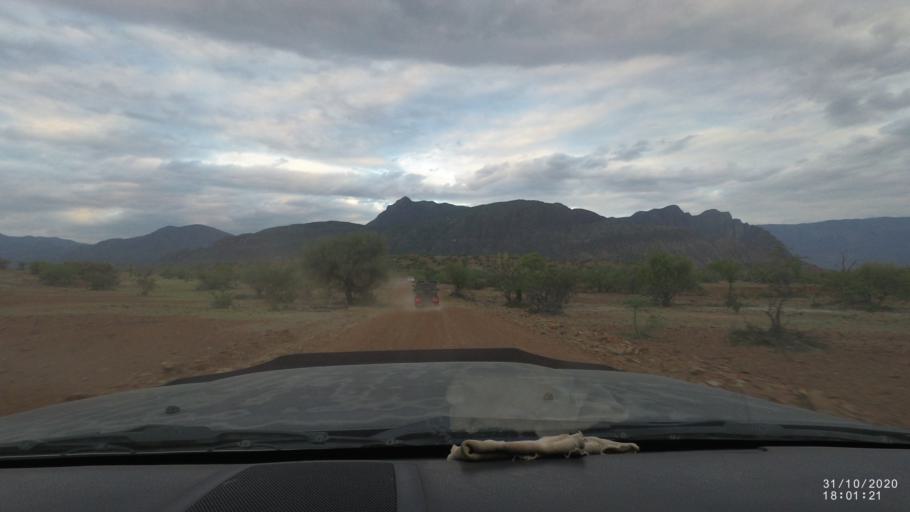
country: BO
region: Chuquisaca
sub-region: Provincia Zudanez
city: Mojocoya
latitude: -18.6645
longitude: -64.5314
